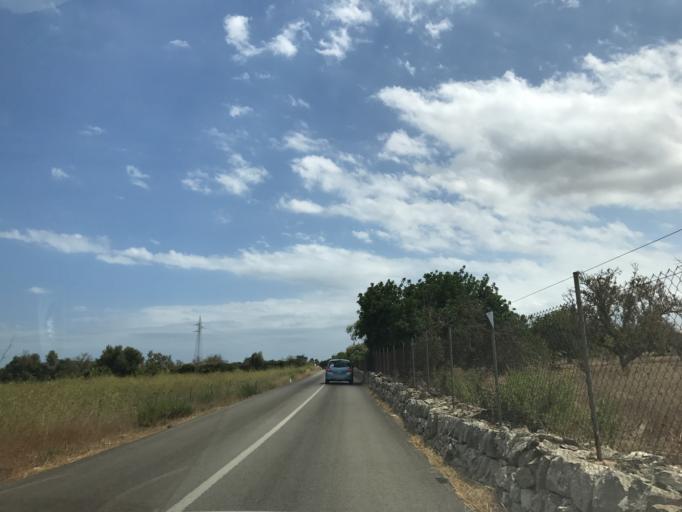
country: ES
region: Balearic Islands
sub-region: Illes Balears
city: Son Servera
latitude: 39.6457
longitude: 3.3460
